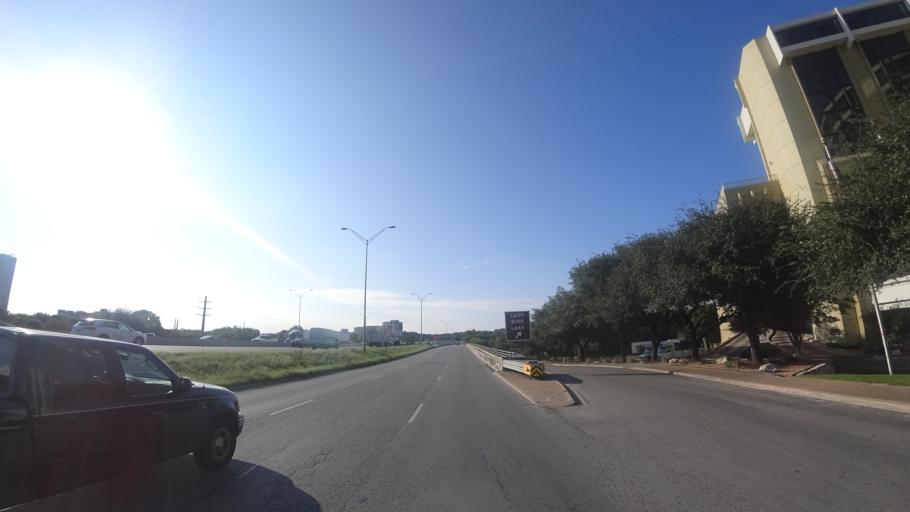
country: US
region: Texas
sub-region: Travis County
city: Austin
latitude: 30.2540
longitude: -97.7370
